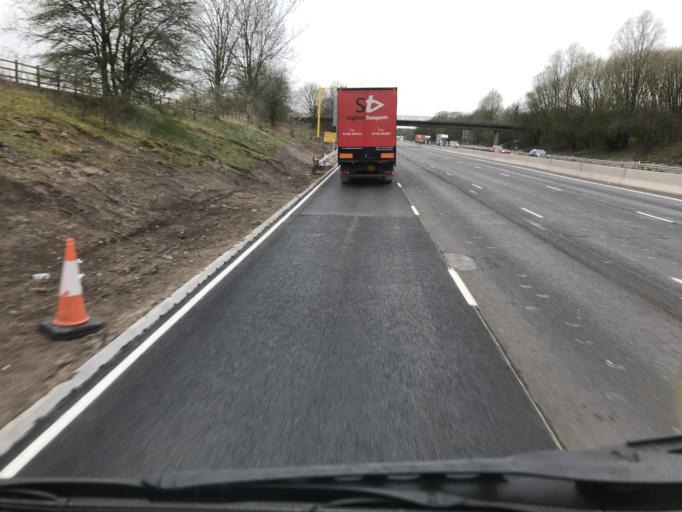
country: GB
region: England
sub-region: City and Borough of Salford
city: Irlam
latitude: 53.4401
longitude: -2.4621
